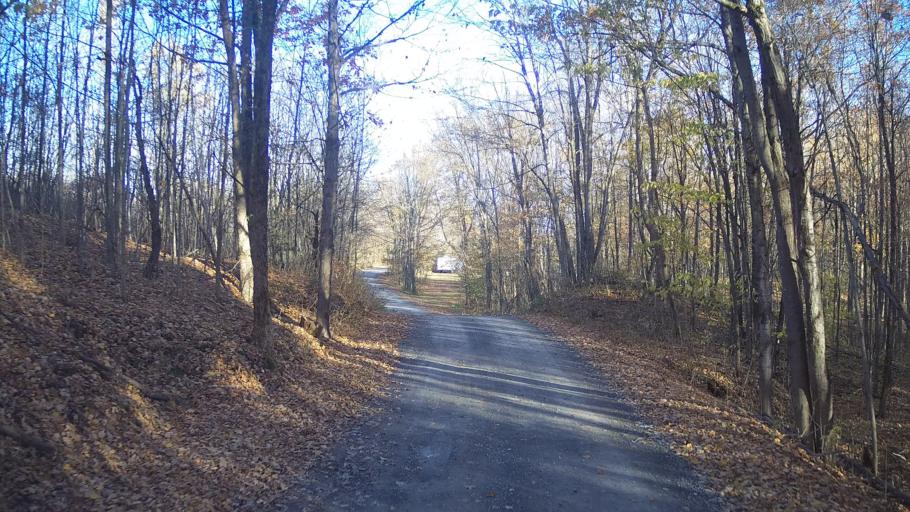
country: CA
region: Ontario
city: Perth
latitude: 44.7448
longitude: -76.4044
